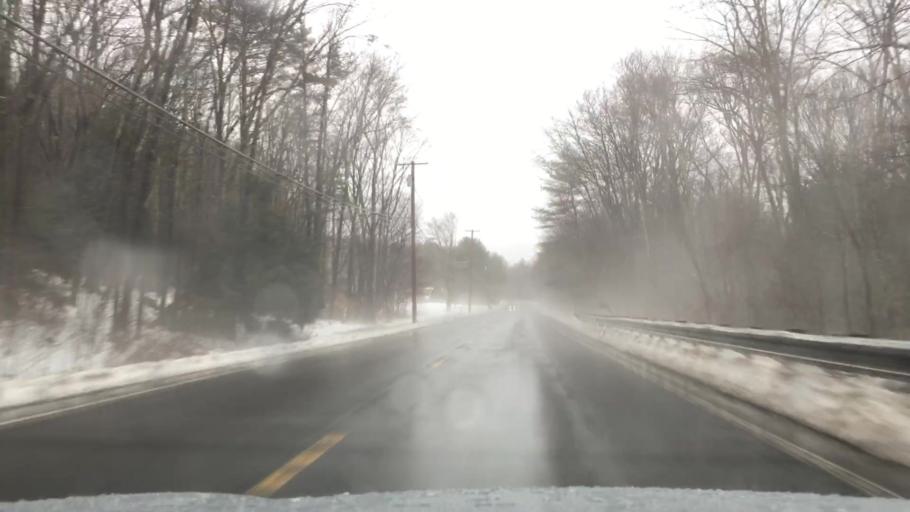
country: US
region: Massachusetts
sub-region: Hampshire County
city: Belchertown
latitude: 42.2993
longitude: -72.4069
